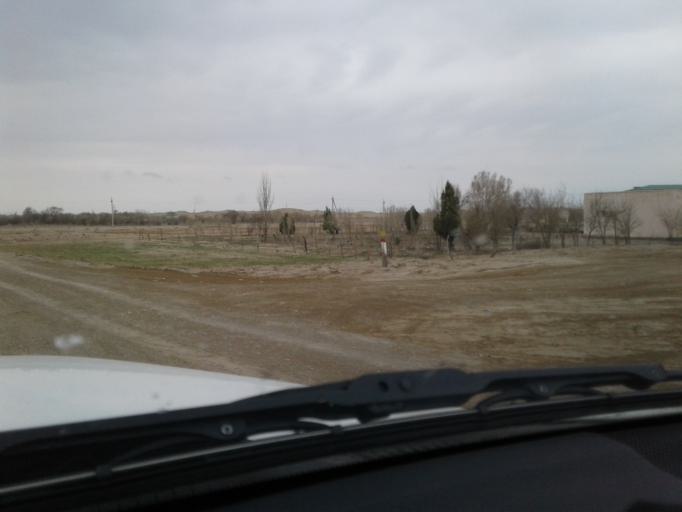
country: TM
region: Ahal
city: Abadan
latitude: 38.7577
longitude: 58.4912
